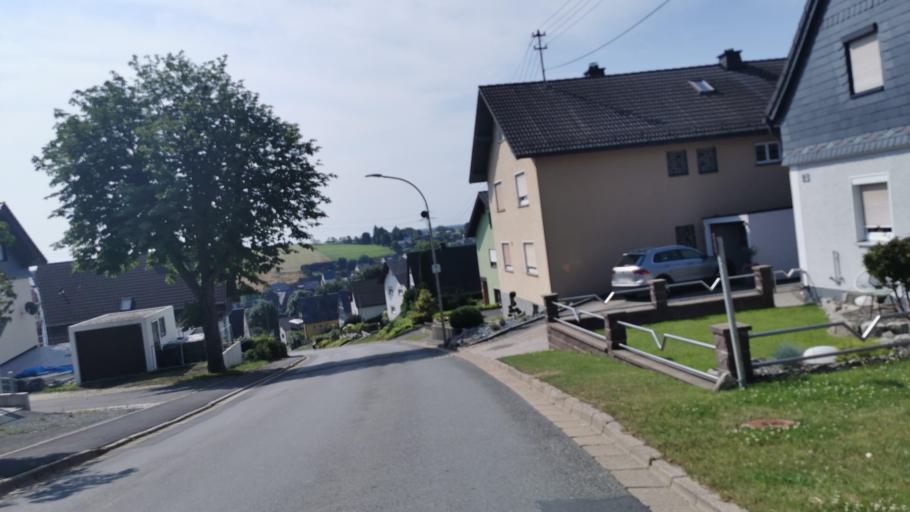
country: DE
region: Bavaria
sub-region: Upper Franconia
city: Tschirn
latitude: 50.3989
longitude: 11.4475
